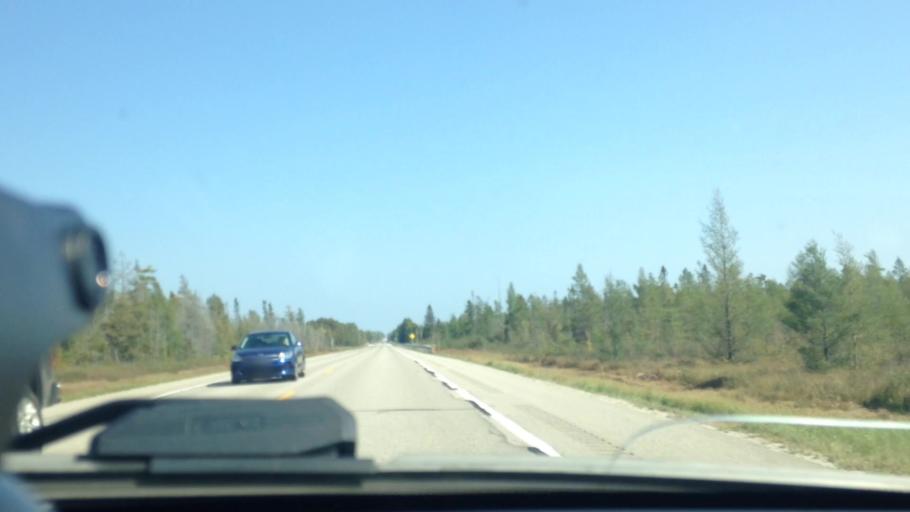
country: US
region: Michigan
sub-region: Luce County
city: Newberry
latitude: 46.3035
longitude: -85.3287
